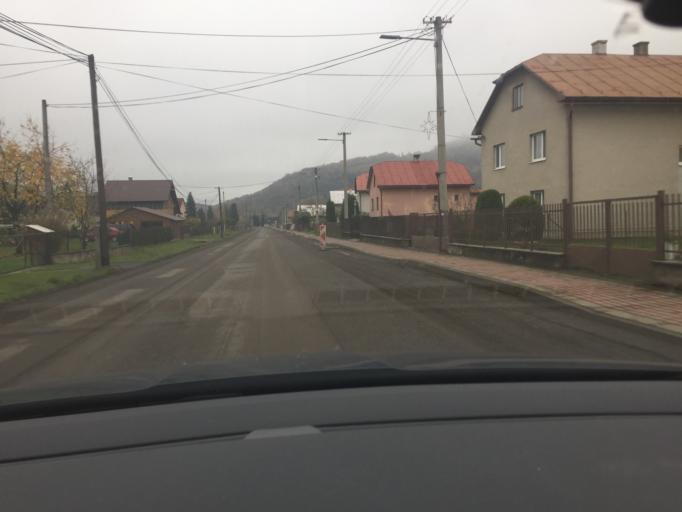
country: PL
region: Lesser Poland Voivodeship
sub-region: Powiat nowosadecki
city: Tylicz
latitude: 49.3066
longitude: 21.0672
